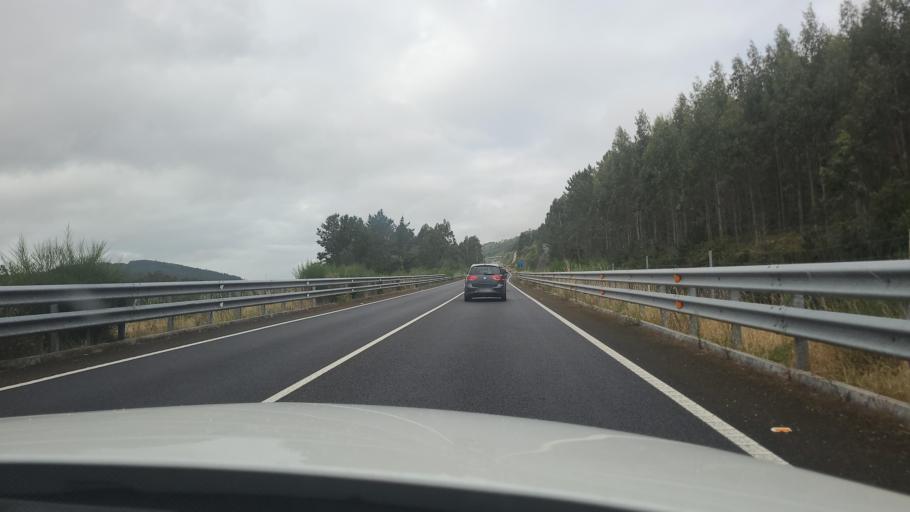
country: ES
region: Galicia
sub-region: Provincia da Coruna
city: Cee
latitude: 42.9745
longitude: -9.1945
